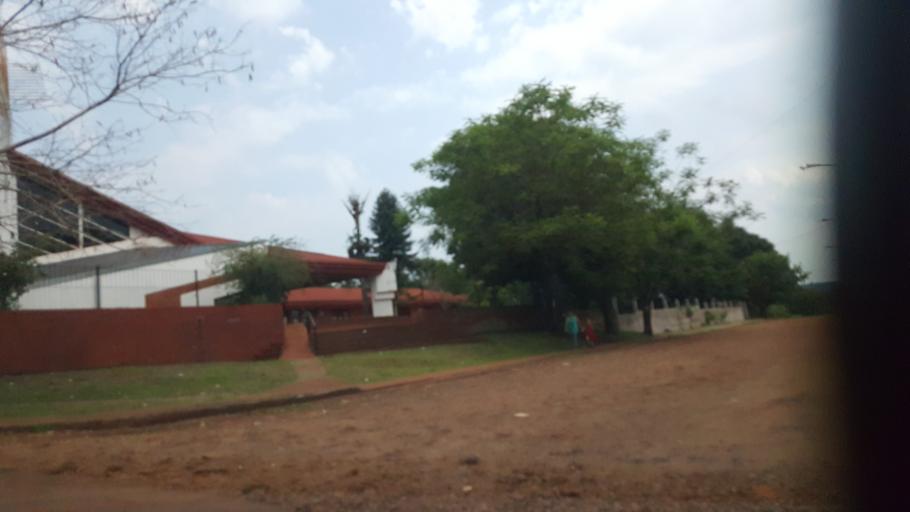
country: AR
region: Misiones
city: Jardin America
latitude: -27.0450
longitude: -55.2450
